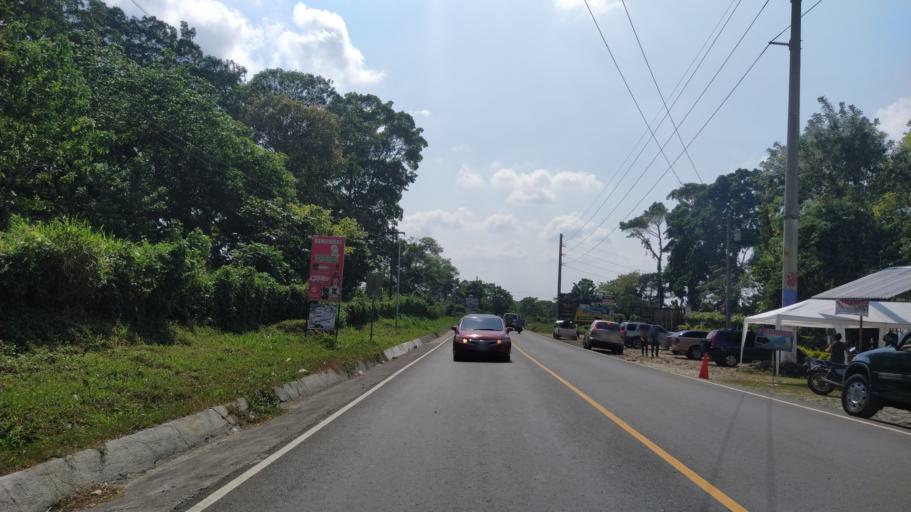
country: GT
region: Retalhuleu
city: San Felipe
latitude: 14.6217
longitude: -91.5861
